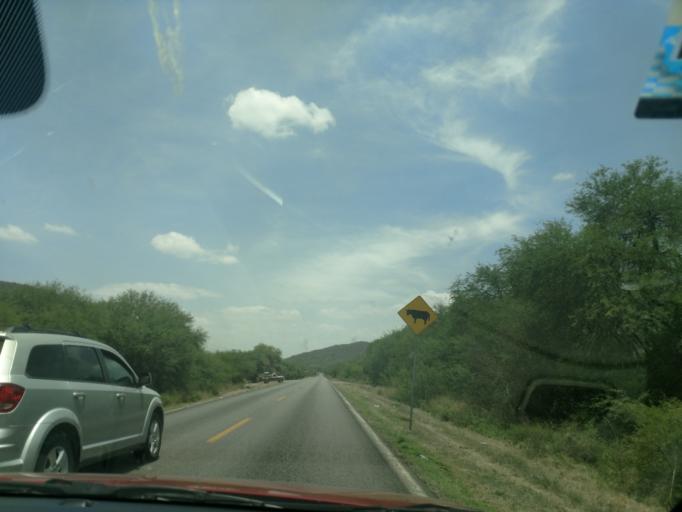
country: MX
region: San Luis Potosi
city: Ciudad Fernandez
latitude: 22.0013
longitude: -100.1432
